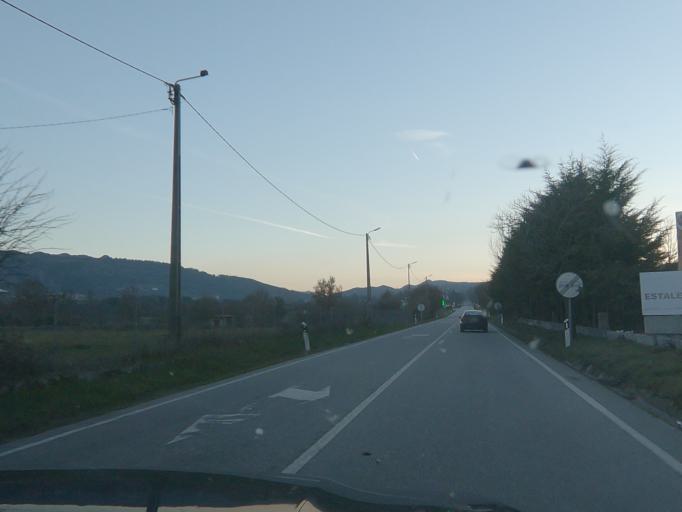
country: PT
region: Vila Real
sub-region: Vila Pouca de Aguiar
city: Vila Pouca de Aguiar
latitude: 41.4378
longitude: -7.6767
